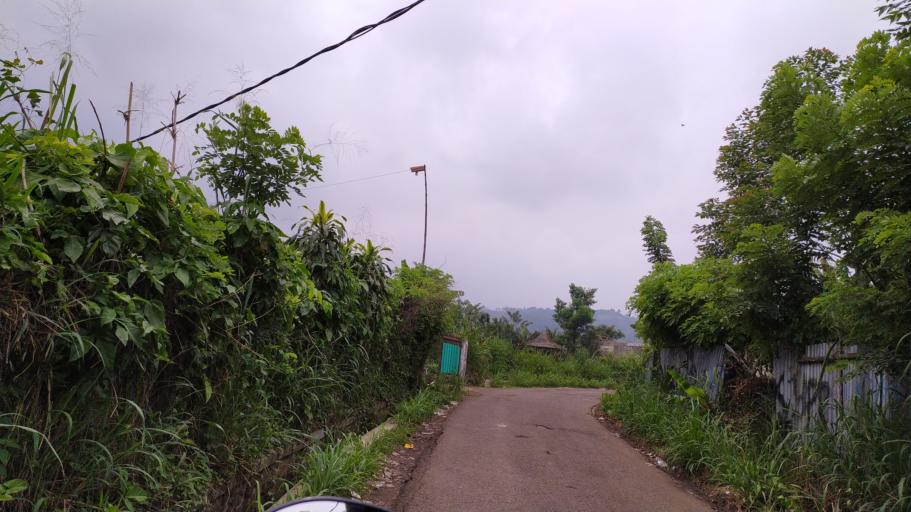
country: ID
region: West Java
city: Ciampea
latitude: -6.6122
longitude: 106.7100
